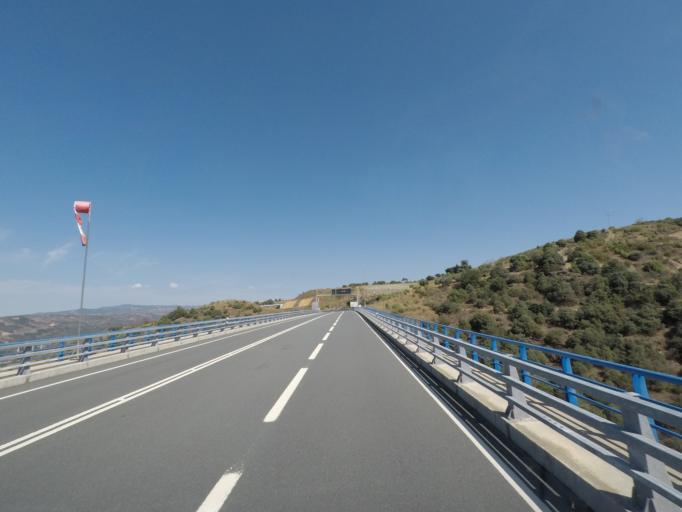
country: PT
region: Braganca
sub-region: Alfandega da Fe
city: Alfandega da Fe
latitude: 41.2838
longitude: -6.8936
